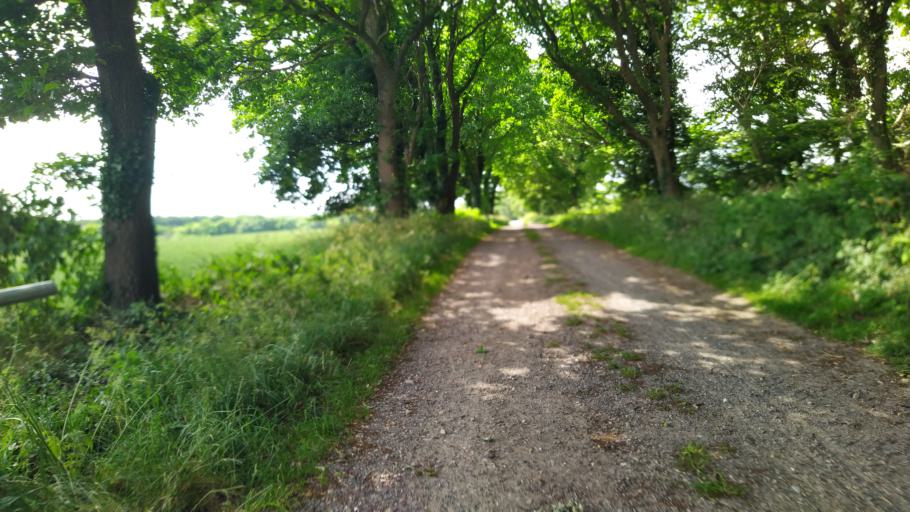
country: DE
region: Lower Saxony
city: Armstorf
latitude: 53.6035
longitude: 9.0763
